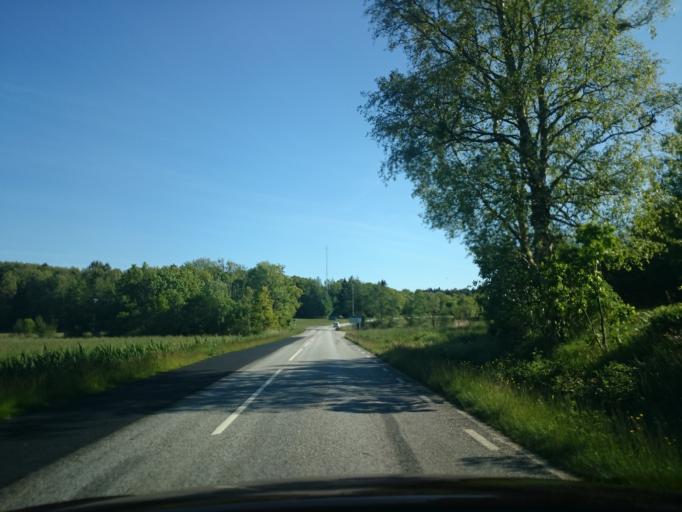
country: SE
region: Vaestra Goetaland
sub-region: Lysekils Kommun
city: Lysekil
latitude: 58.2636
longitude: 11.5381
